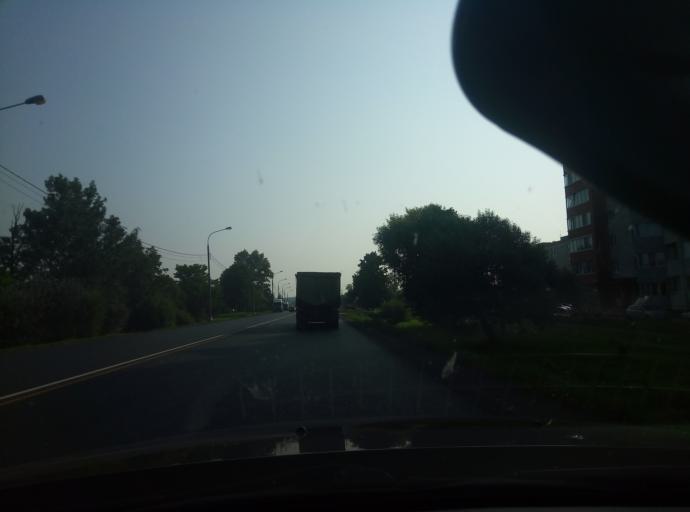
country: RU
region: Kaluga
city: Belousovo
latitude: 55.0902
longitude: 36.6595
